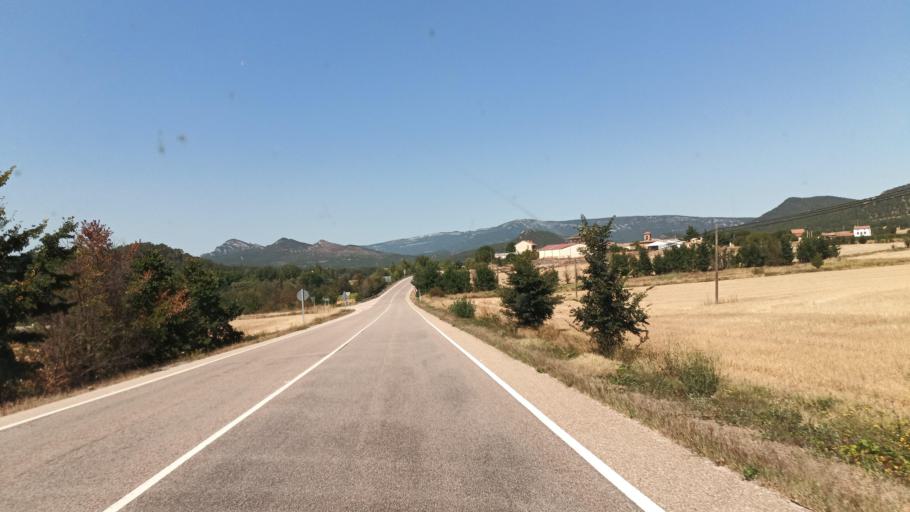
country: ES
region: Castille and Leon
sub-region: Provincia de Burgos
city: Salas de Bureba
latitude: 42.6777
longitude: -3.4246
